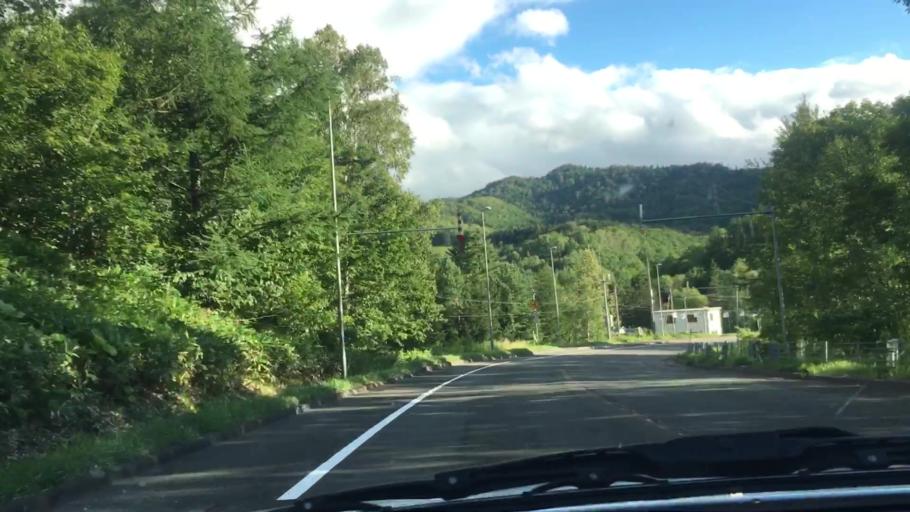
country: JP
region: Hokkaido
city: Shimo-furano
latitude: 43.1256
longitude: 142.6777
